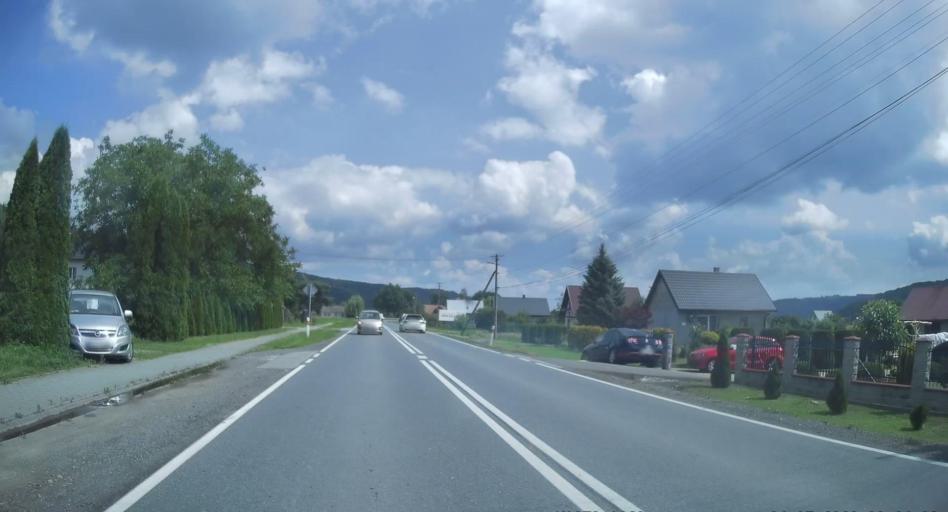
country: PL
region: Lesser Poland Voivodeship
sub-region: Powiat tarnowski
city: Wielka Wies
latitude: 49.9016
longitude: 20.8154
